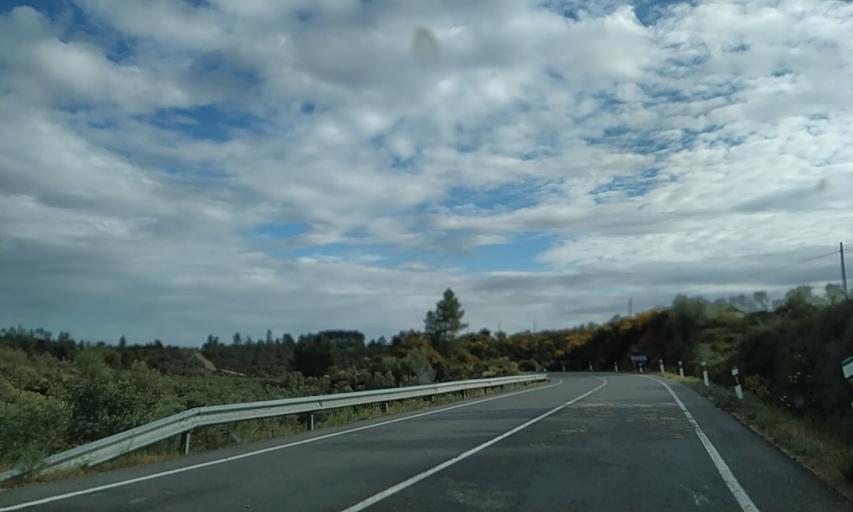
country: ES
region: Extremadura
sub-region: Provincia de Caceres
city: Perales del Puerto
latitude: 40.1461
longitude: -6.6765
